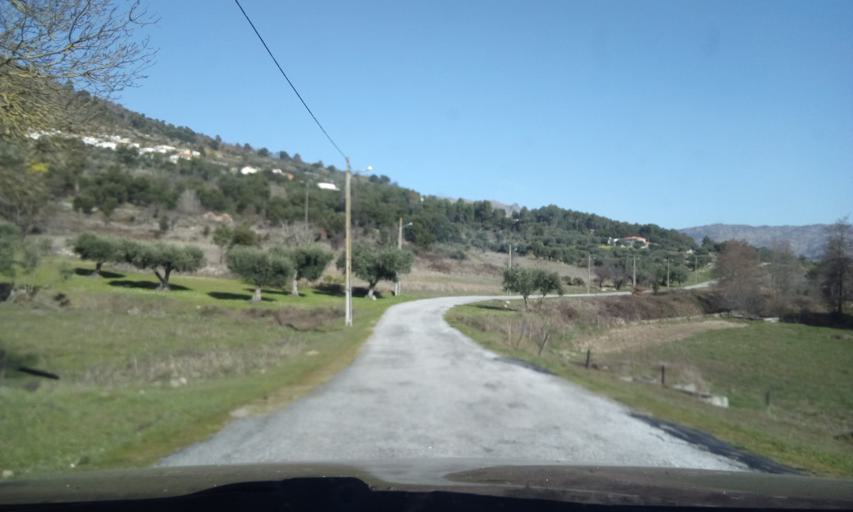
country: PT
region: Guarda
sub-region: Celorico da Beira
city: Celorico da Beira
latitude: 40.6869
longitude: -7.4545
